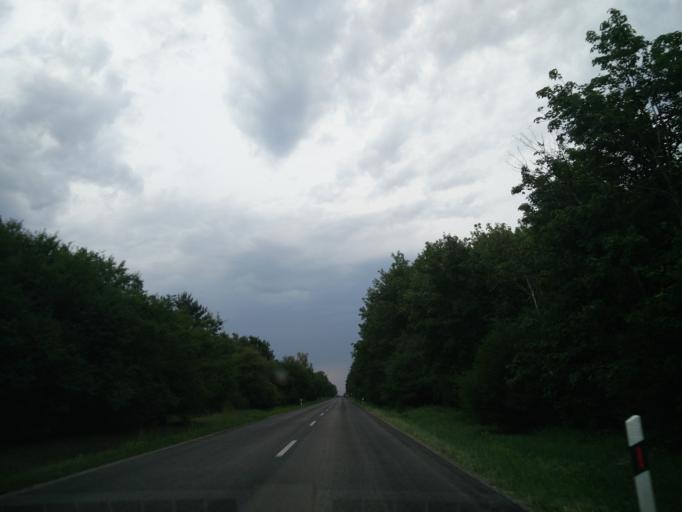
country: HU
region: Vas
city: Vasvar
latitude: 47.0313
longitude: 16.8139
